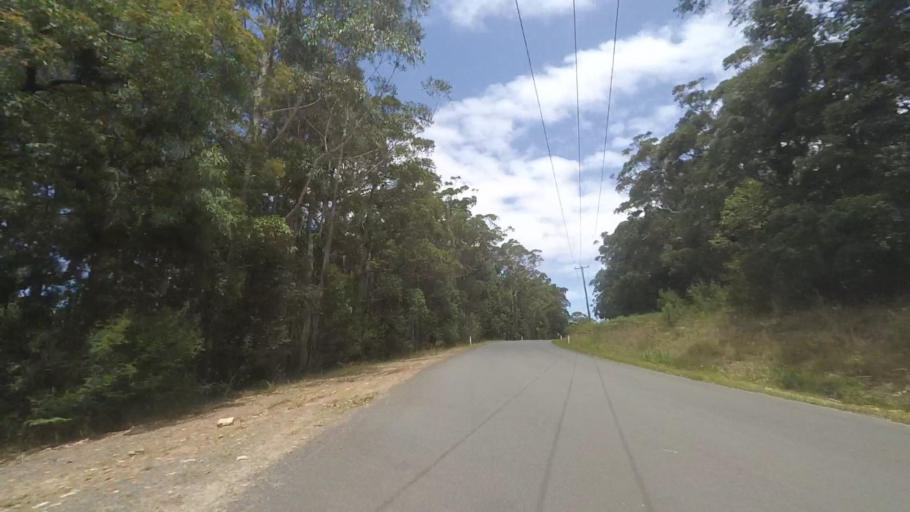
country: AU
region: New South Wales
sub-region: Shoalhaven Shire
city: Milton
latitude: -35.3926
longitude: 150.3688
